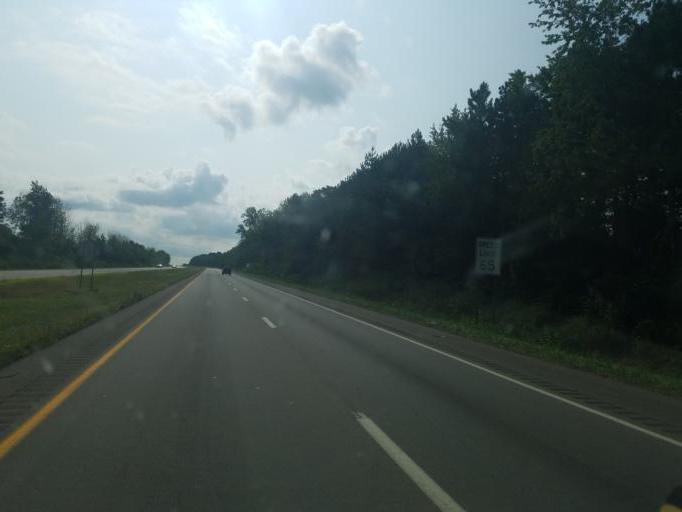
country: US
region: Ohio
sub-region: Wayne County
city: Dalton
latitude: 40.7961
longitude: -81.6474
